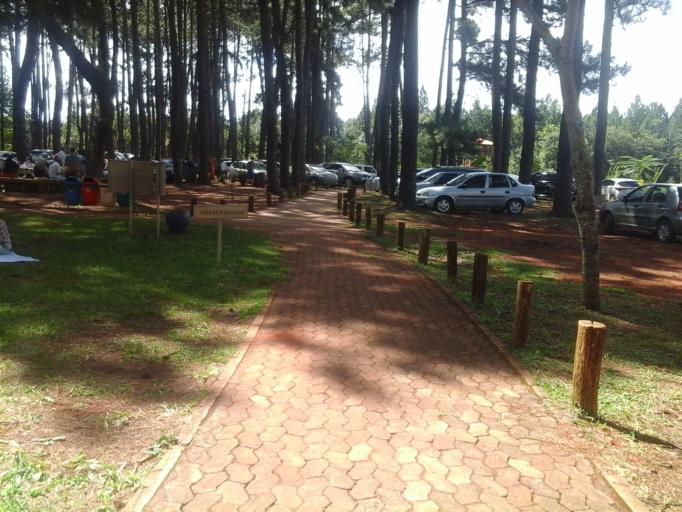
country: BR
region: Federal District
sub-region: Brasilia
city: Brasilia
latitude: -15.8736
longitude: -47.8351
